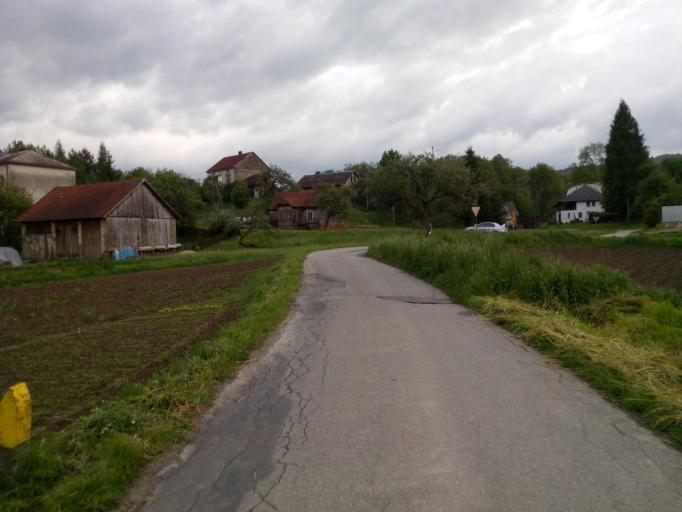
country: PL
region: Subcarpathian Voivodeship
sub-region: Powiat strzyzowski
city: Strzyzow
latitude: 49.8229
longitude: 21.8336
